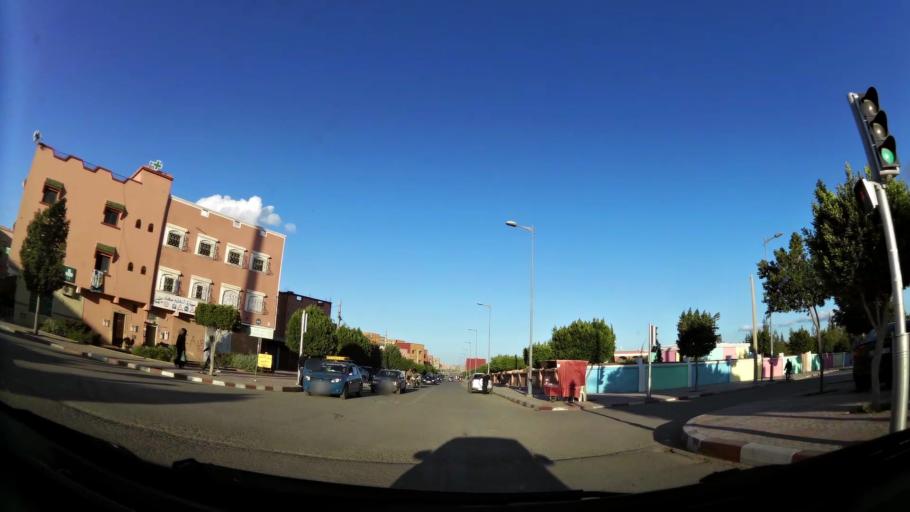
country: MA
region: Marrakech-Tensift-Al Haouz
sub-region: Kelaa-Des-Sraghna
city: Sidi Abdallah
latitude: 32.2395
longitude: -7.9535
